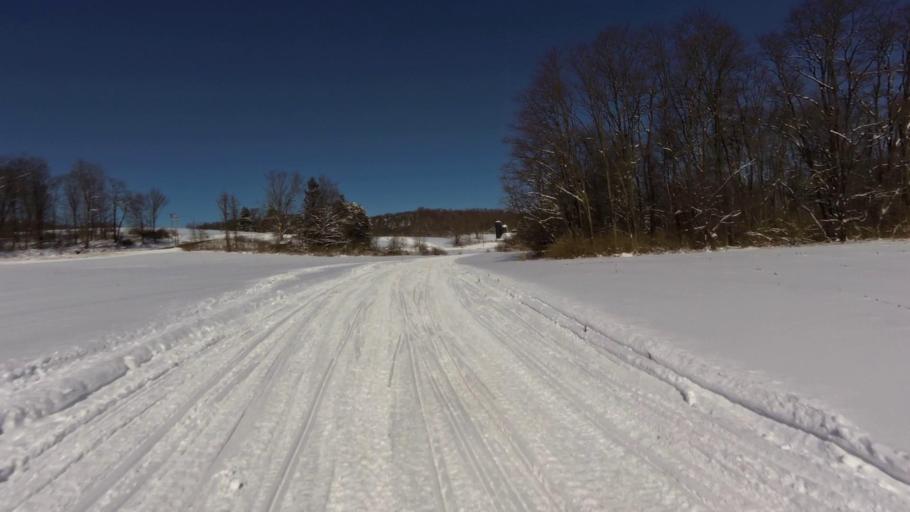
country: US
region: New York
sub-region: Chautauqua County
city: Mayville
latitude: 42.2486
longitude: -79.4405
